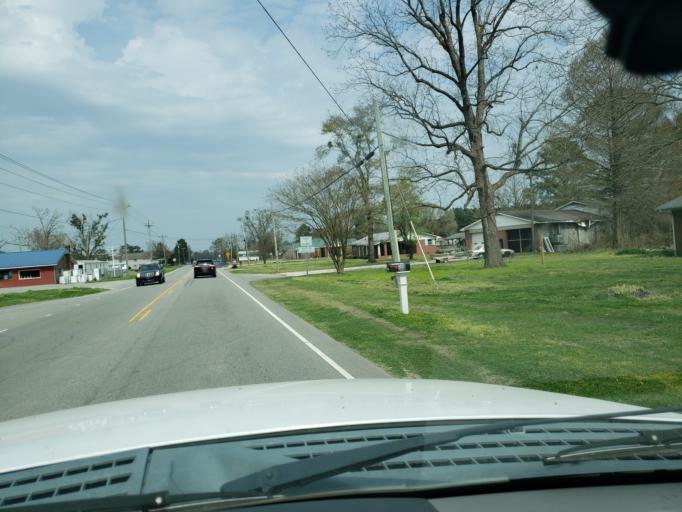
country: US
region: North Carolina
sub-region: Duplin County
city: Wallace
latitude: 34.7791
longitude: -77.9123
